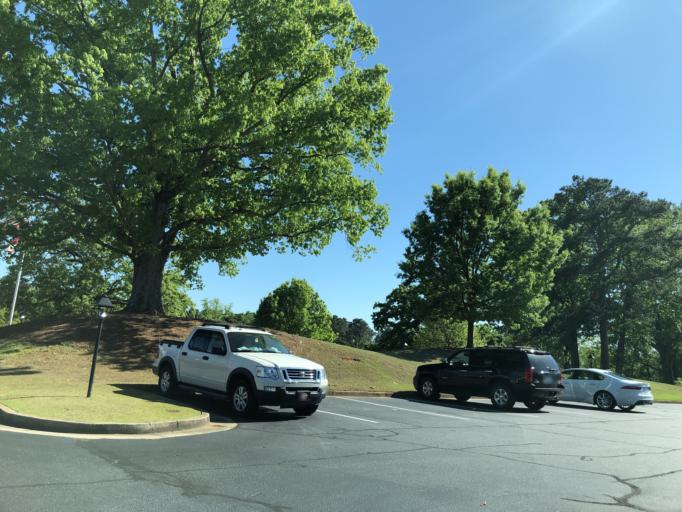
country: US
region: Georgia
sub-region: Clarke County
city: Country Club Estates
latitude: 33.9780
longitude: -83.4124
